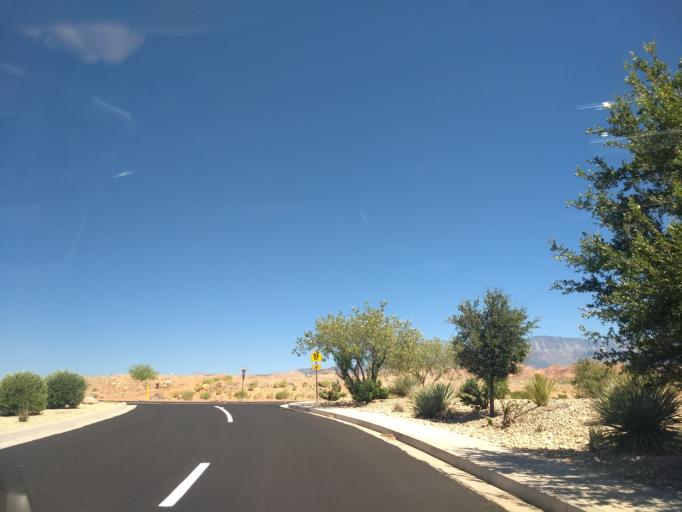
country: US
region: Utah
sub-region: Washington County
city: Washington
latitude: 37.1491
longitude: -113.4653
